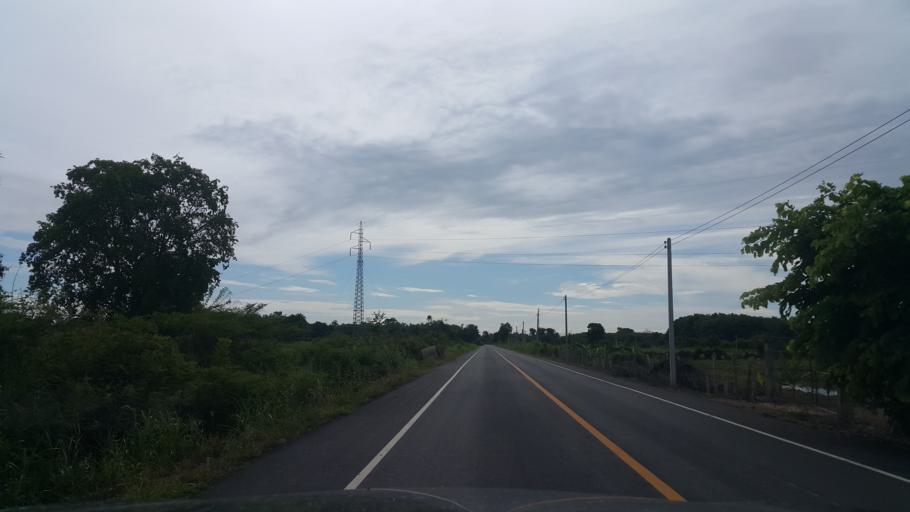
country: TH
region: Sukhothai
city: Si Nakhon
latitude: 17.2718
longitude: 99.9512
